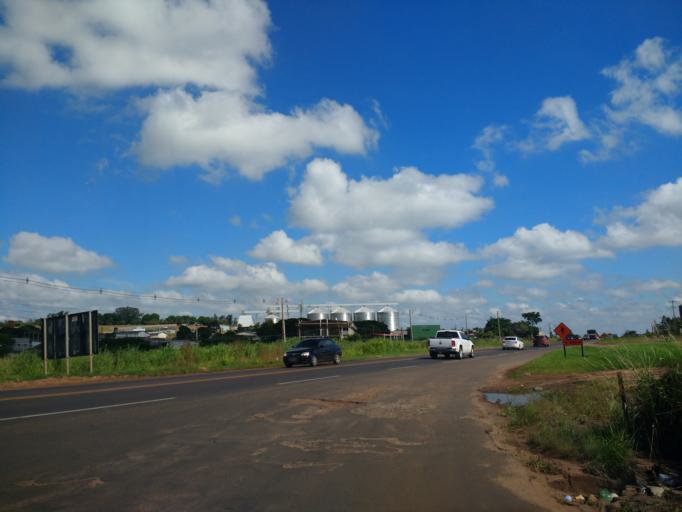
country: BR
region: Parana
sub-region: Umuarama
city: Umuarama
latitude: -23.8101
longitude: -53.3235
